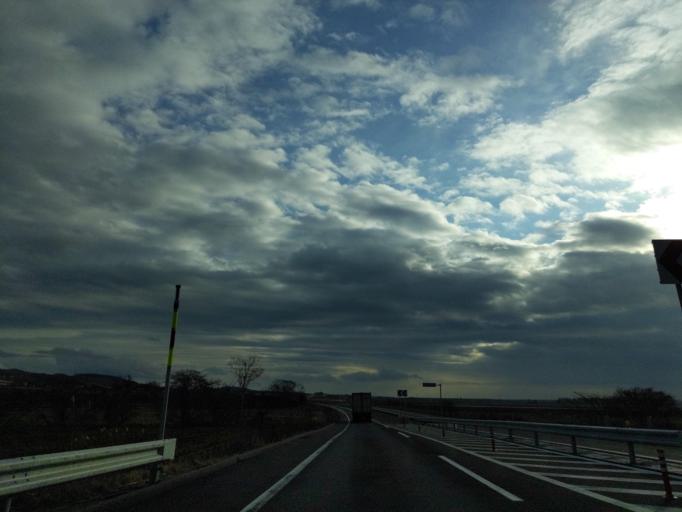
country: JP
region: Hokkaido
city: Chitose
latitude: 42.9450
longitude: 141.7137
